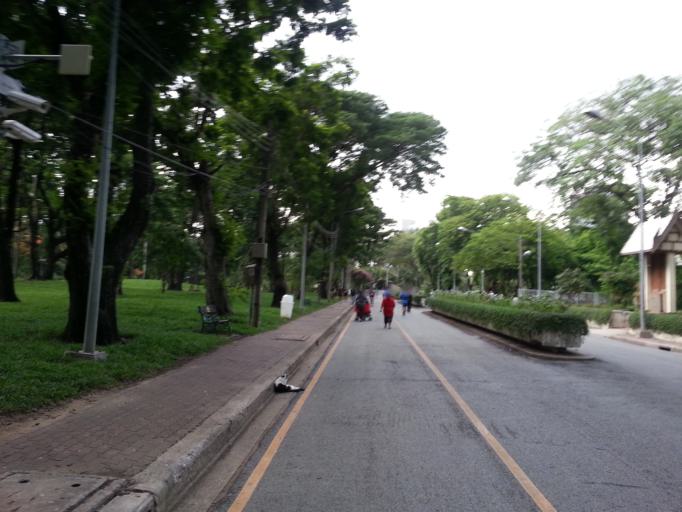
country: TH
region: Bangkok
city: Bang Rak
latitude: 13.7320
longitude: 100.5435
